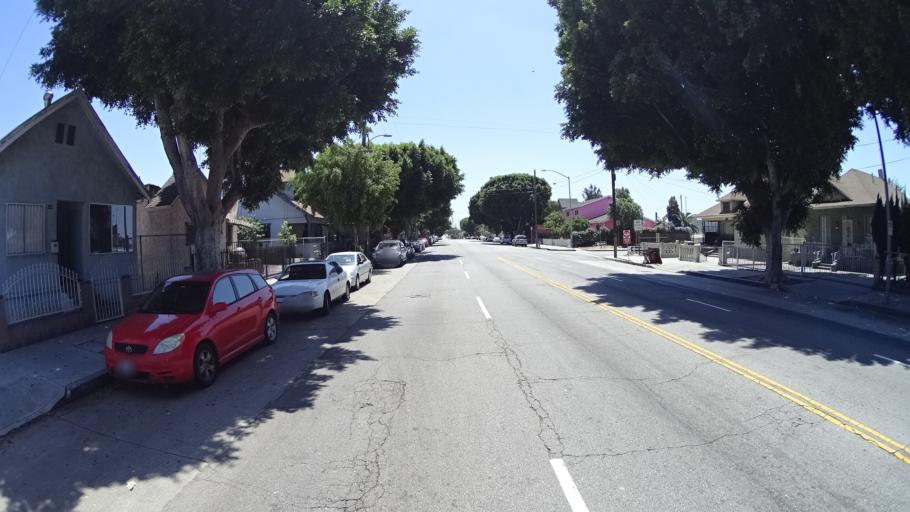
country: US
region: California
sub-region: Los Angeles County
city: Los Angeles
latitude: 34.0690
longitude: -118.2155
